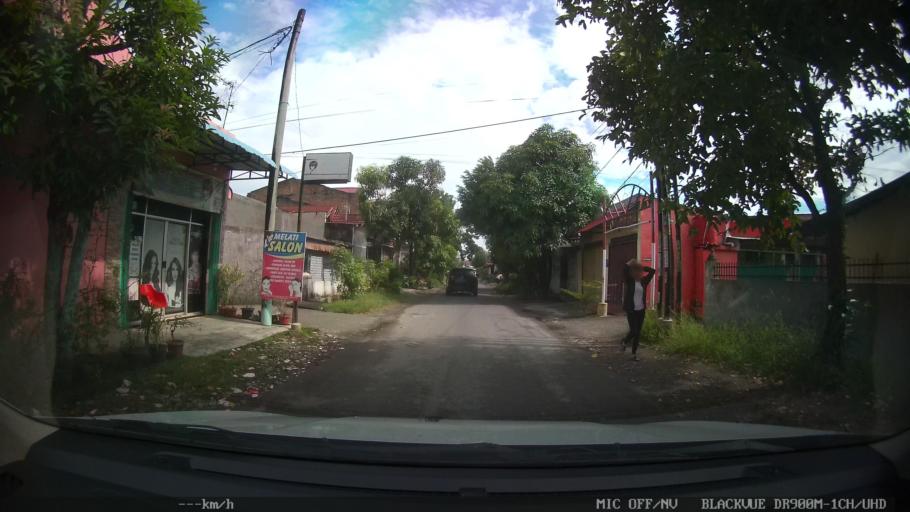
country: ID
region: North Sumatra
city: Sunggal
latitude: 3.6110
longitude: 98.6294
